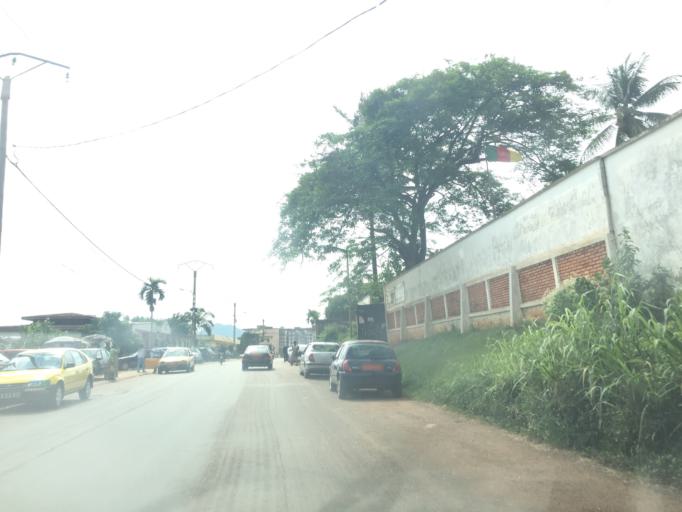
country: CM
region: Centre
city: Yaounde
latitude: 3.8766
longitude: 11.5207
